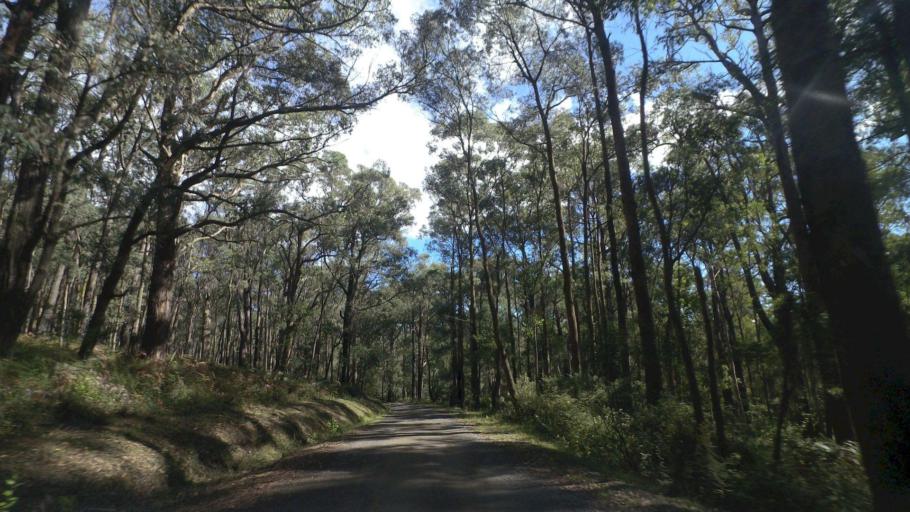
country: AU
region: Victoria
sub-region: Cardinia
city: Gembrook
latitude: -37.9250
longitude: 145.6001
